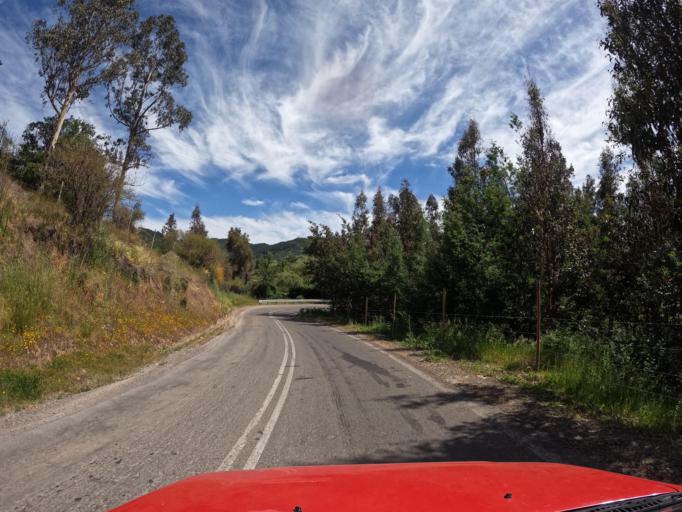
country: CL
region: Maule
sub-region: Provincia de Talca
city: Talca
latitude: -34.9920
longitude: -71.8539
